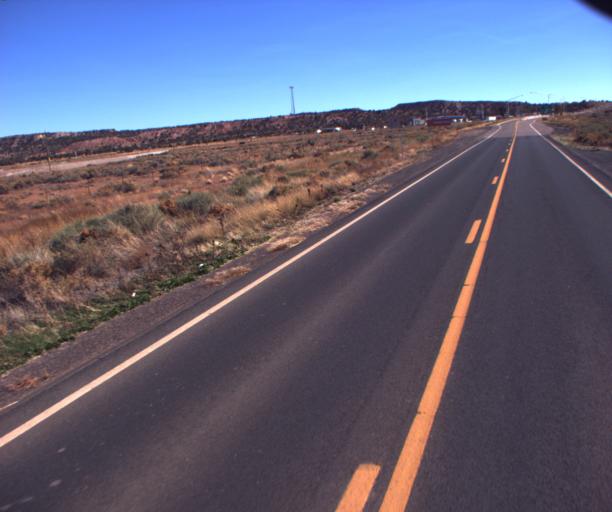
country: US
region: Arizona
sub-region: Apache County
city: Ganado
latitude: 35.7573
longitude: -109.6303
